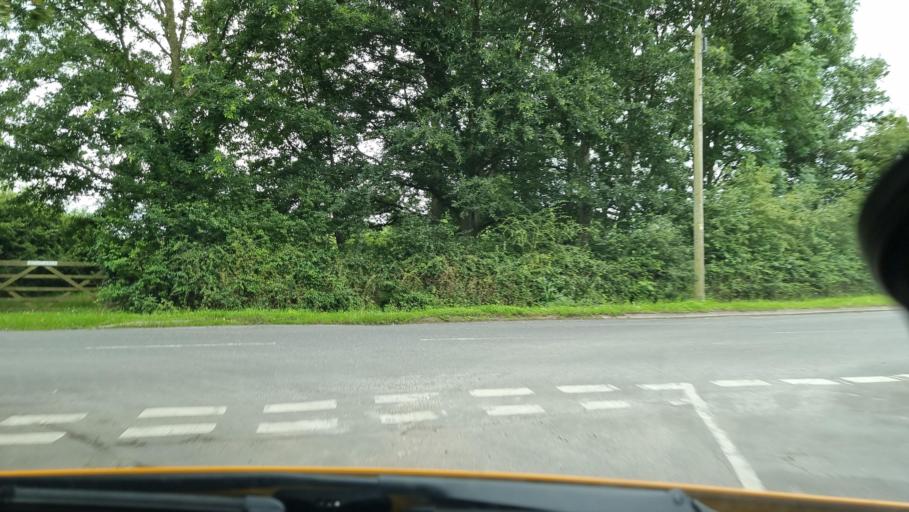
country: GB
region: England
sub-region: Oxfordshire
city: North Leigh
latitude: 51.8143
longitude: -1.4567
